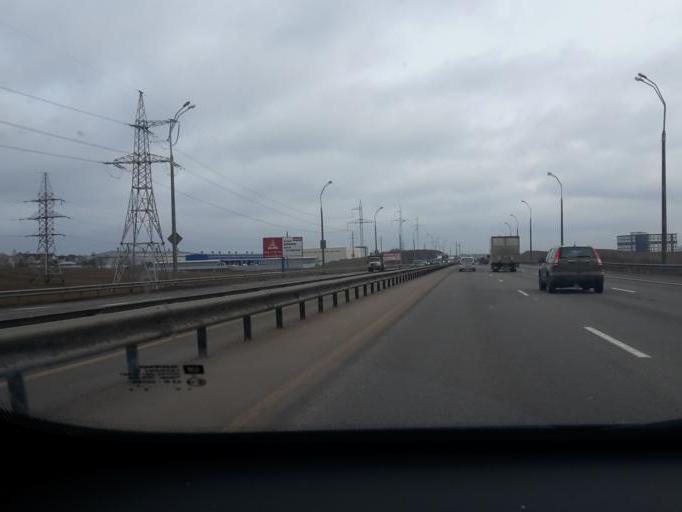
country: BY
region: Minsk
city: Zhdanovichy
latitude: 53.9287
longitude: 27.4199
